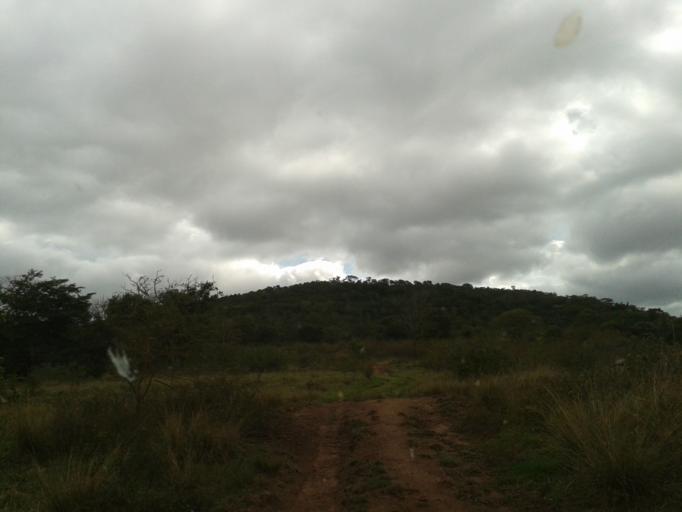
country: BR
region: Minas Gerais
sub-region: Campina Verde
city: Campina Verde
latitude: -19.4628
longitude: -49.5898
